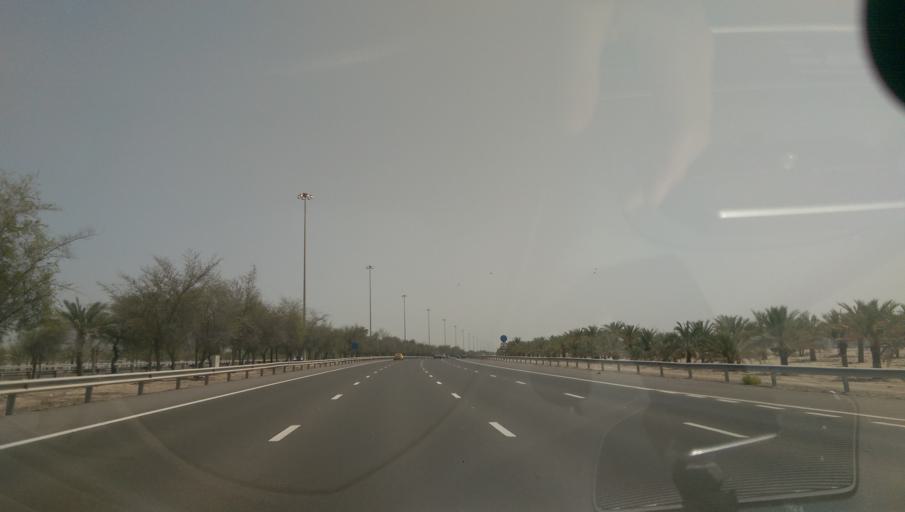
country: AE
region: Abu Dhabi
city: Abu Dhabi
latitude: 24.4855
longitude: 54.6757
